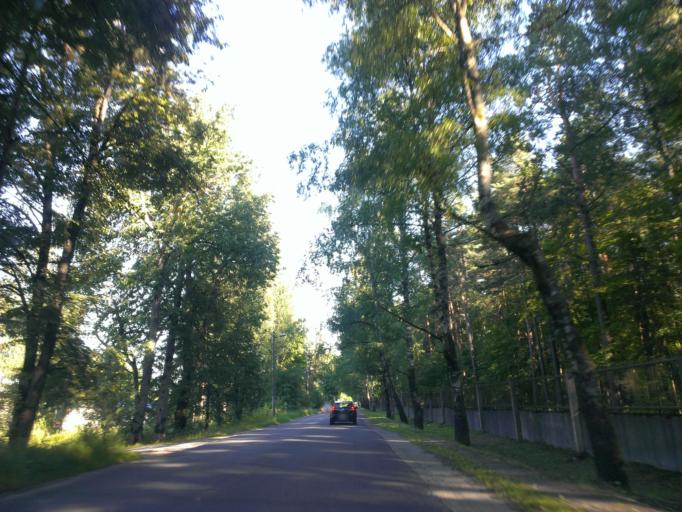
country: LV
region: Riga
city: Bergi
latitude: 56.9932
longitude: 24.2854
